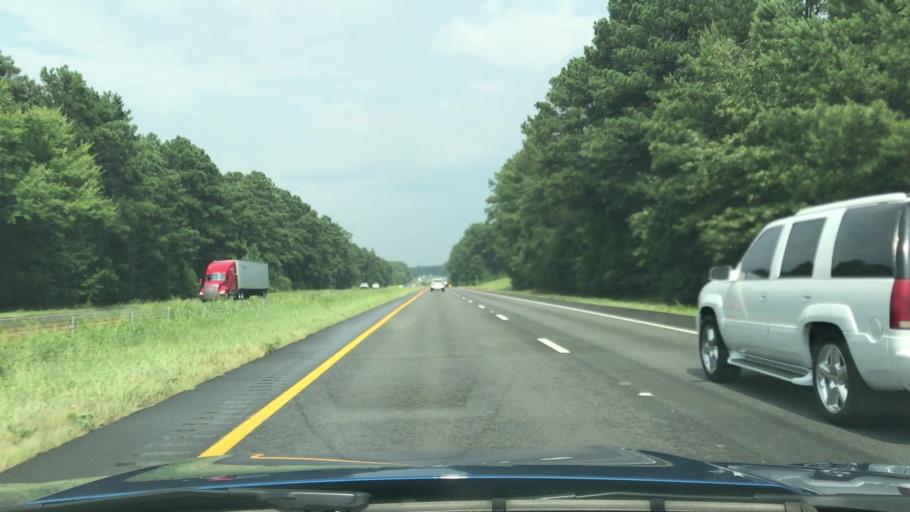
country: US
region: Texas
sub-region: Harrison County
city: Hallsville
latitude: 32.4808
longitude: -94.5417
